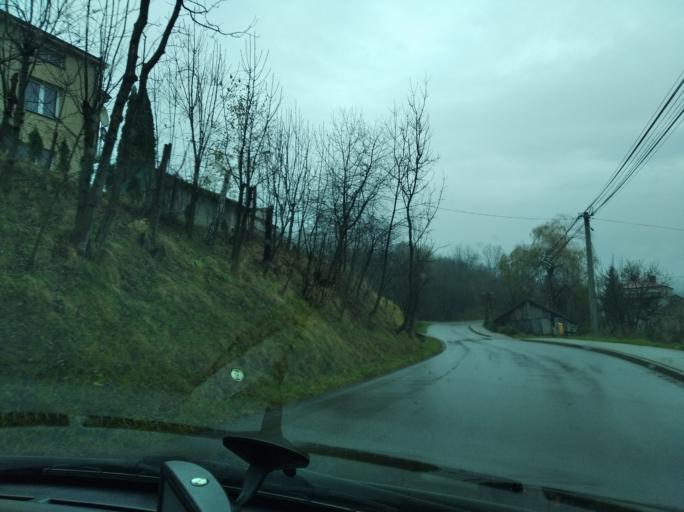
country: PL
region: Subcarpathian Voivodeship
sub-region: Powiat rzeszowski
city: Lubenia
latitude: 49.9280
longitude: 21.9287
